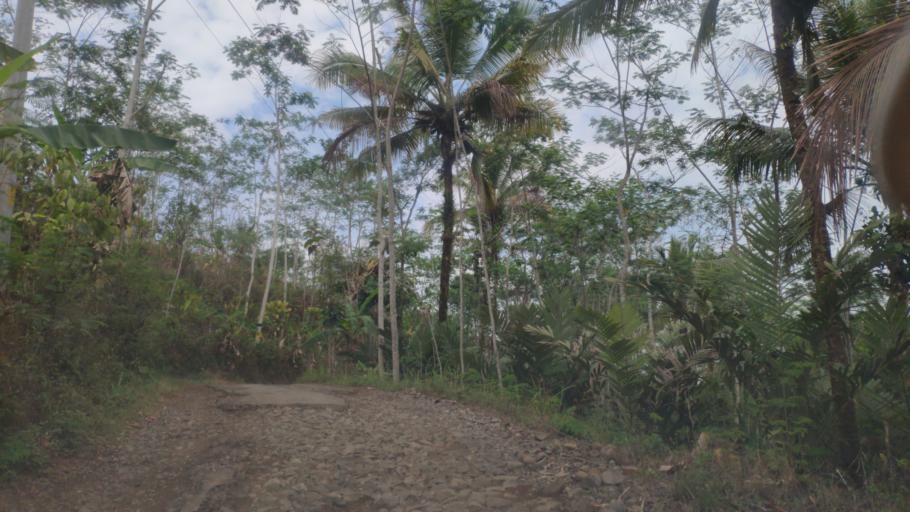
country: ID
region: Central Java
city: Wonosobo
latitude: -7.4483
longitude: 109.8253
